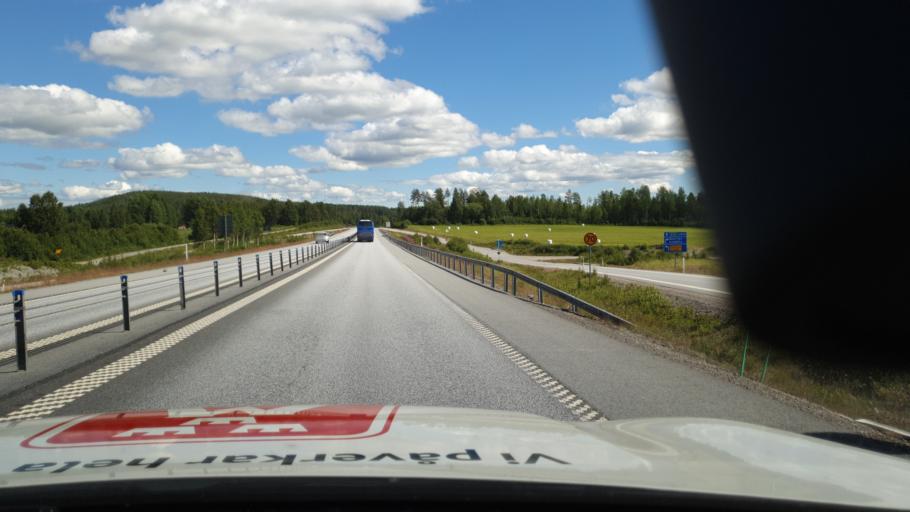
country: SE
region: Vaesterbotten
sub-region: Vannas Kommun
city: Vannasby
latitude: 63.8937
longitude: 19.9504
